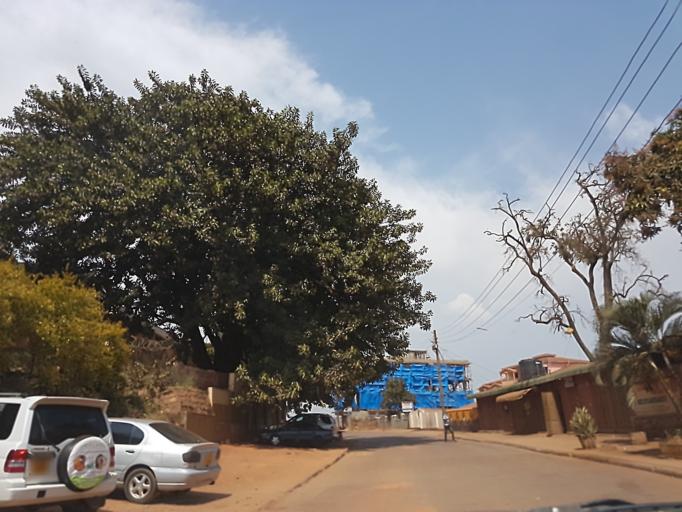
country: UG
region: Central Region
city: Kampala Central Division
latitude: 0.3135
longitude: 32.5692
